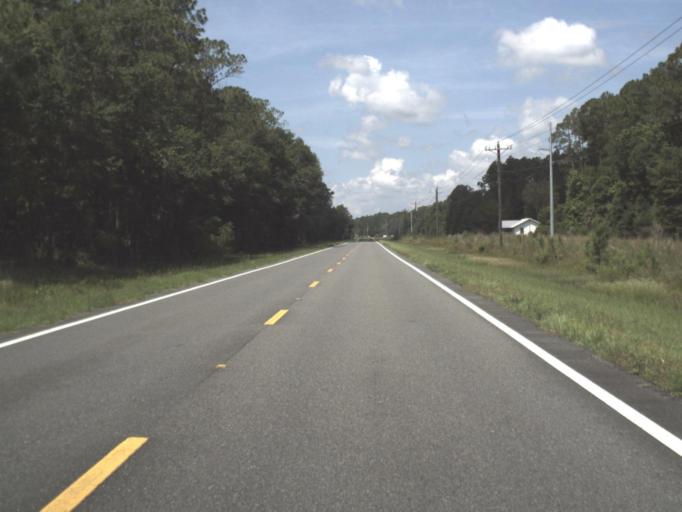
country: US
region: Florida
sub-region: Levy County
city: Chiefland
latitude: 29.3167
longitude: -82.7882
